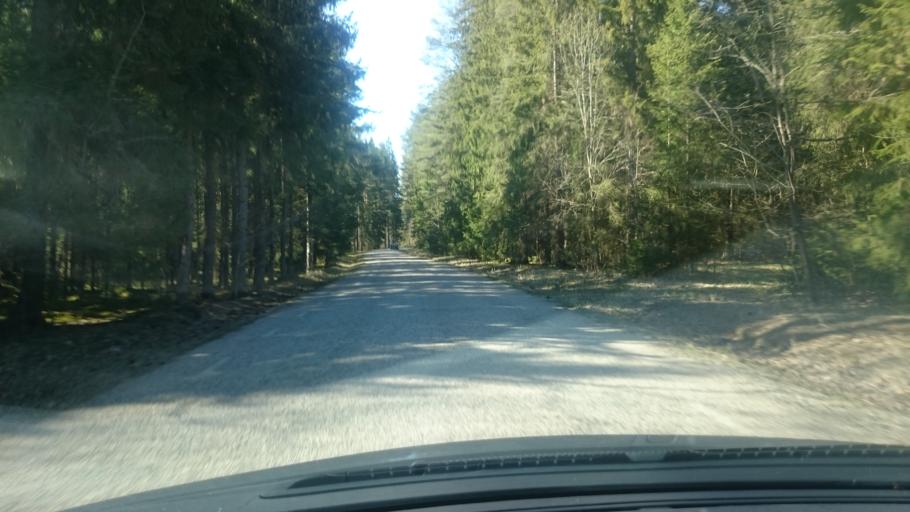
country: EE
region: Polvamaa
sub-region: Polva linn
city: Polva
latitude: 58.1260
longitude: 27.0184
